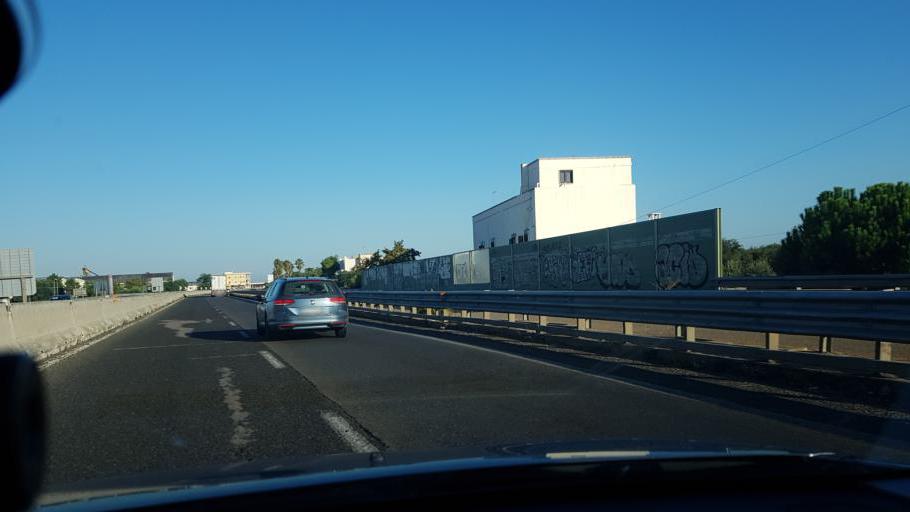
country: IT
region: Apulia
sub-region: Provincia di Brindisi
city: Fasano
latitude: 40.8555
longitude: 17.3526
